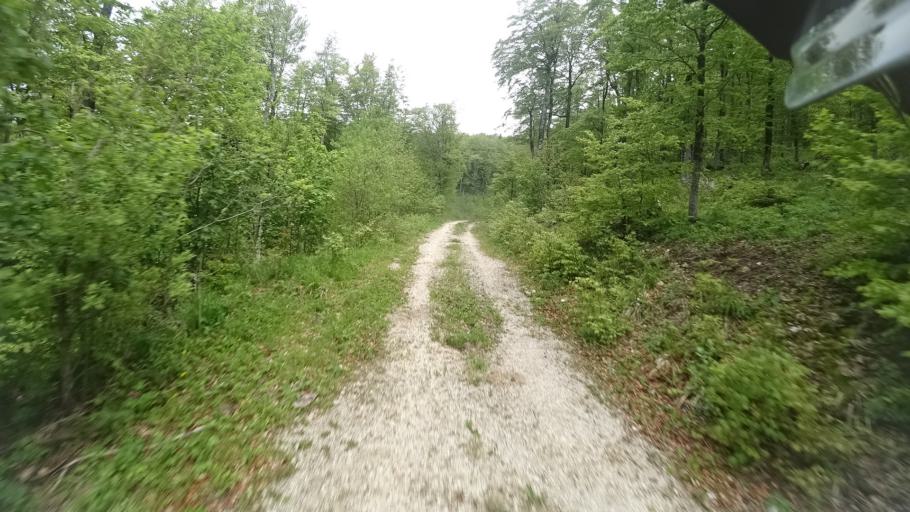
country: BA
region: Federation of Bosnia and Herzegovina
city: Orasac
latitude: 44.5730
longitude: 15.8695
